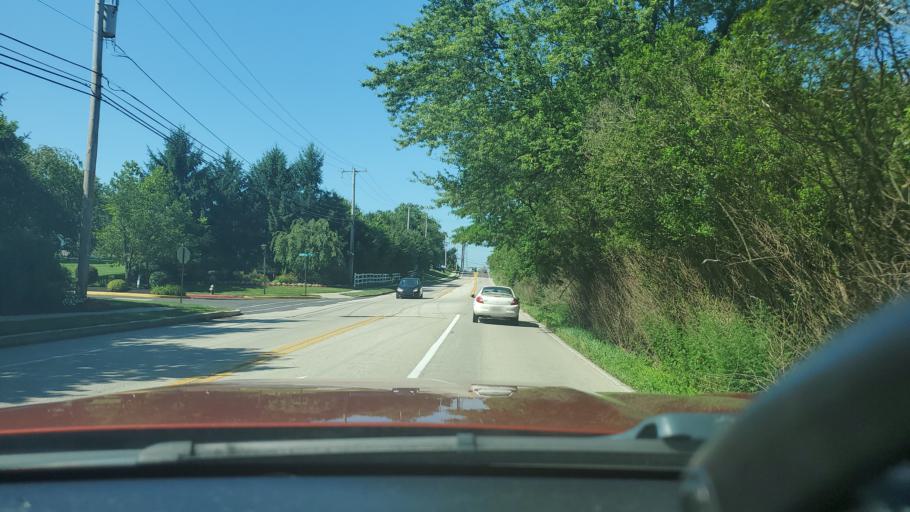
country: US
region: Pennsylvania
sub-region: Montgomery County
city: Limerick
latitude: 40.2259
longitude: -75.5362
